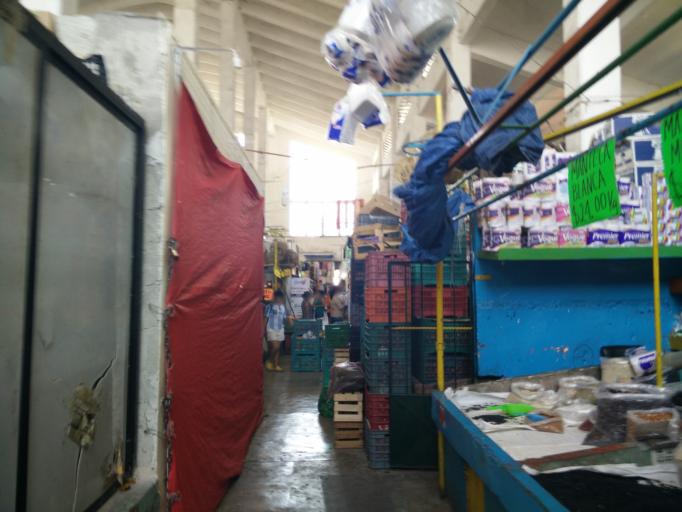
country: MX
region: Veracruz
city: Coatepec
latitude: 19.4547
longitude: -96.9616
